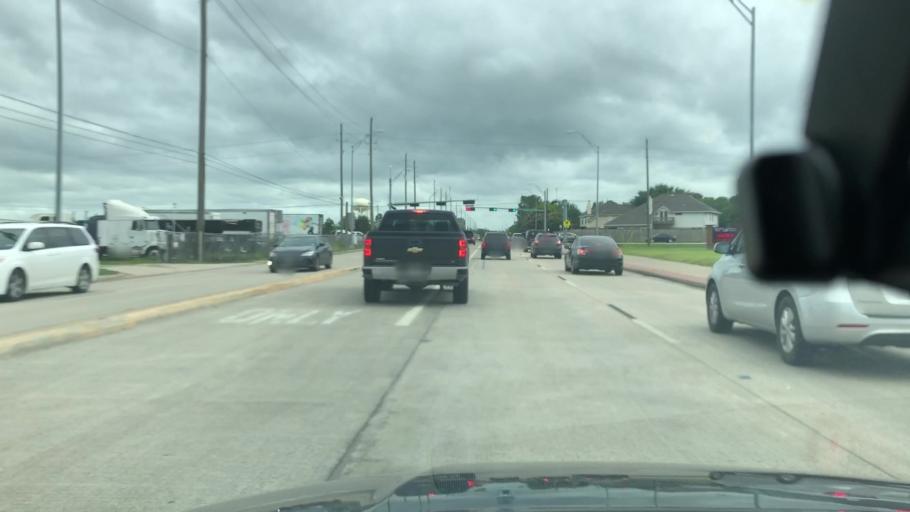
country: US
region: Texas
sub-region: Brazoria County
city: Brookside Village
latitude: 29.5718
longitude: -95.3508
